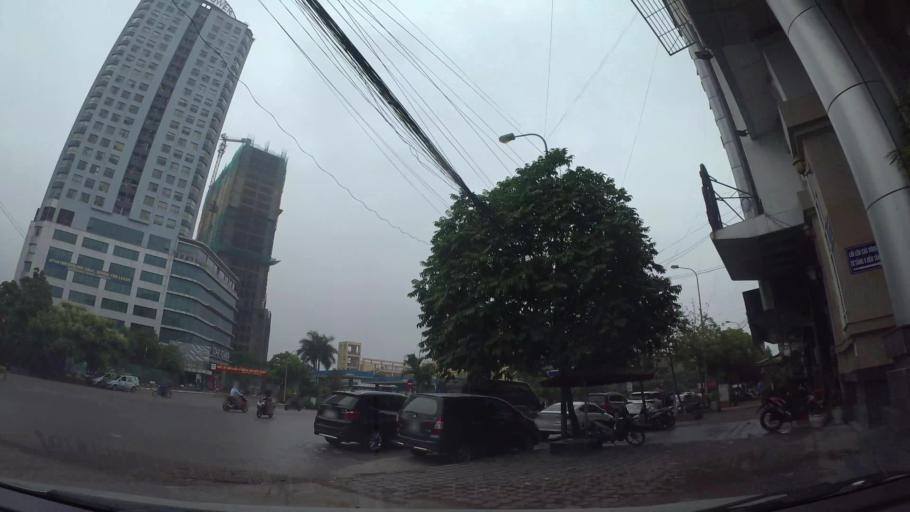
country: VN
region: Ha Noi
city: Cau Giay
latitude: 21.0241
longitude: 105.7919
